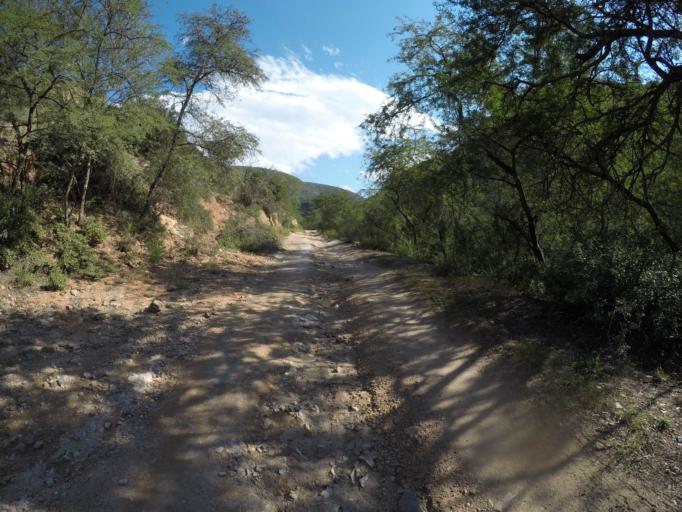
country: ZA
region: Eastern Cape
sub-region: Cacadu District Municipality
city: Kareedouw
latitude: -33.6546
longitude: 24.3642
